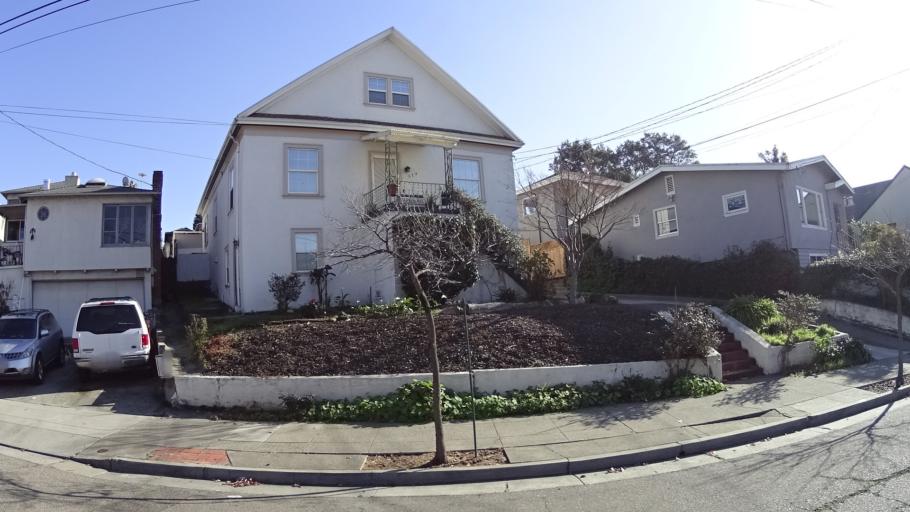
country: US
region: California
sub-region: Alameda County
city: Piedmont
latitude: 37.8054
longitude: -122.2439
